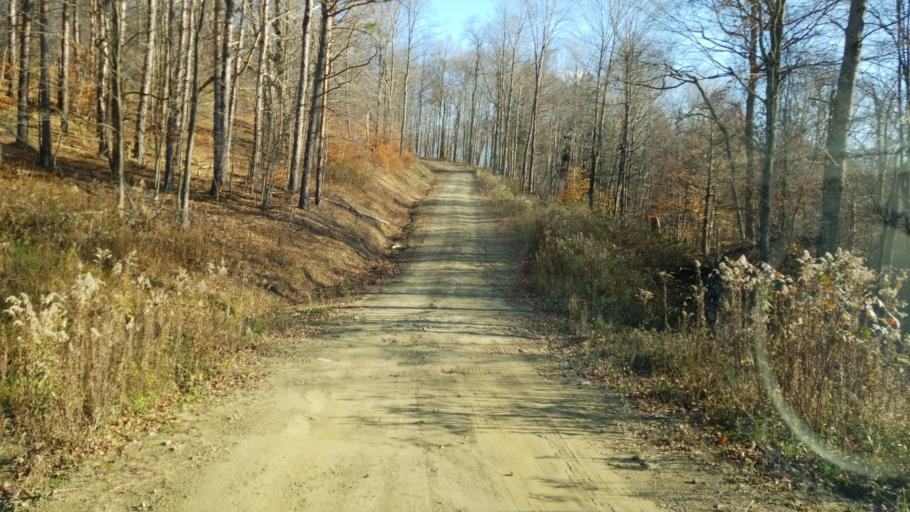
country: US
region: Pennsylvania
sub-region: Clearfield County
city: Treasure Lake
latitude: 41.1573
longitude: -78.6574
